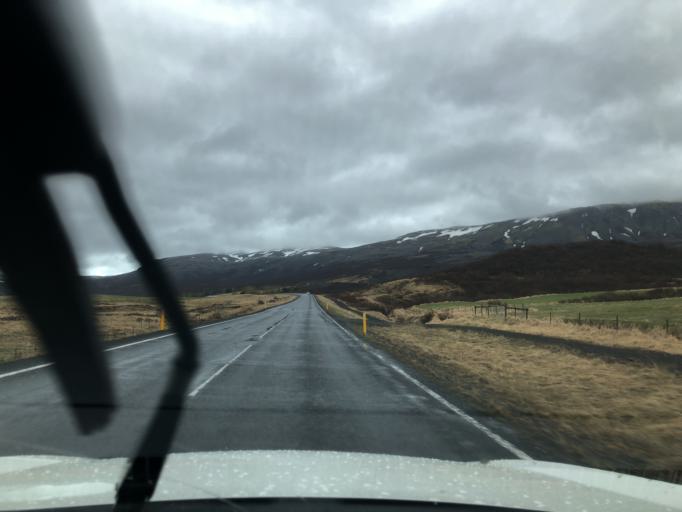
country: IS
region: South
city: Selfoss
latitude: 64.2270
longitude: -20.6330
